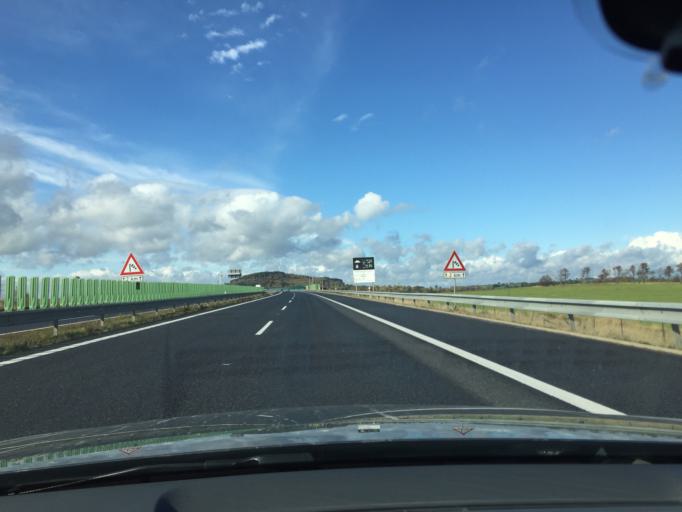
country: CZ
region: Ustecky
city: Chlumec
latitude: 50.7728
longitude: 13.9516
